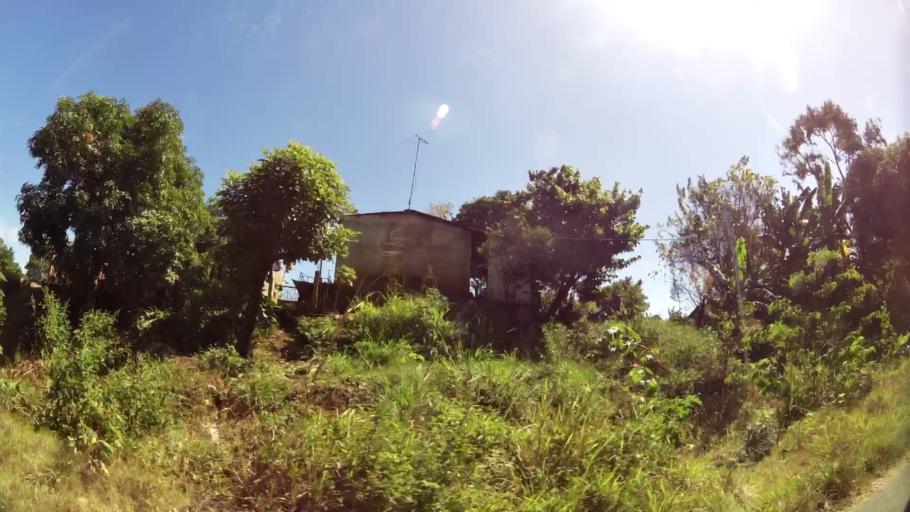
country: SV
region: Ahuachapan
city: Ahuachapan
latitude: 13.9329
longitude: -89.8410
